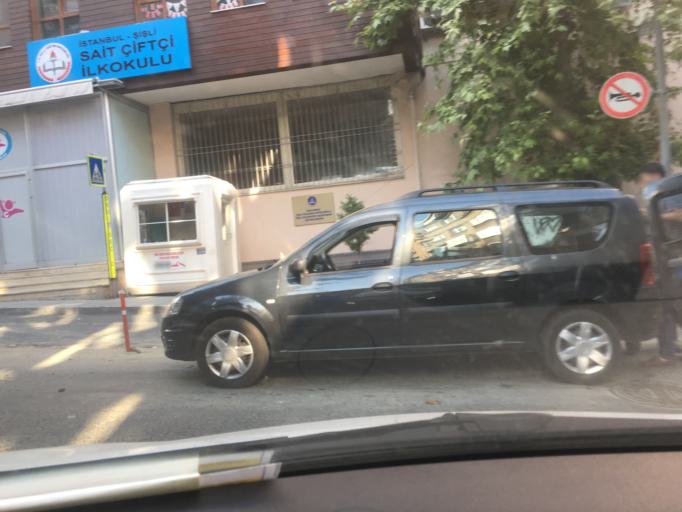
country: TR
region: Istanbul
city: Sisli
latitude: 41.0495
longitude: 28.9957
